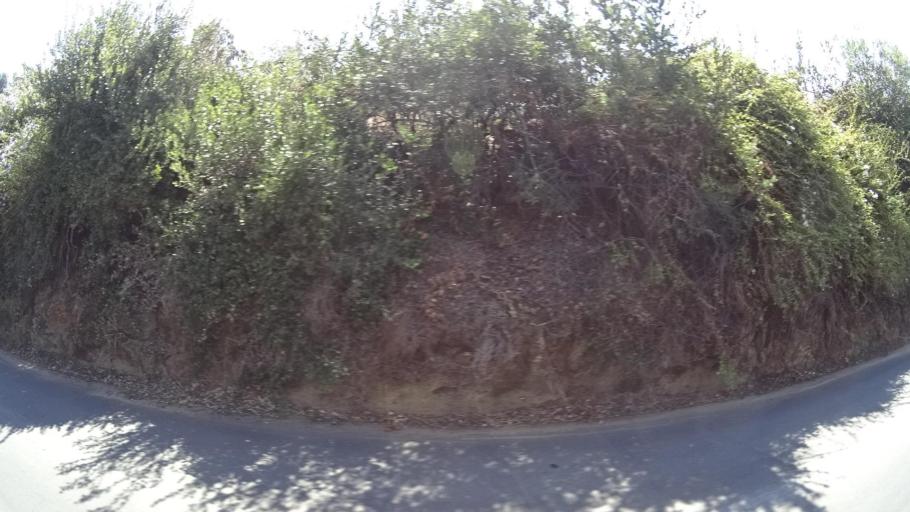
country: US
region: California
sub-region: San Diego County
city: Lake San Marcos
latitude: 33.1661
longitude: -117.2109
